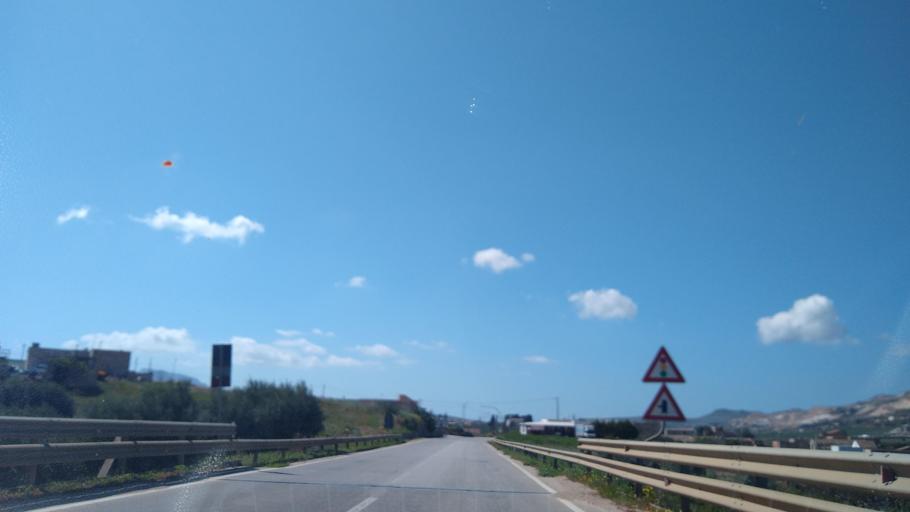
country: IT
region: Sicily
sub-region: Trapani
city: Buseto Palizzolo
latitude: 38.0288
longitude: 12.7270
